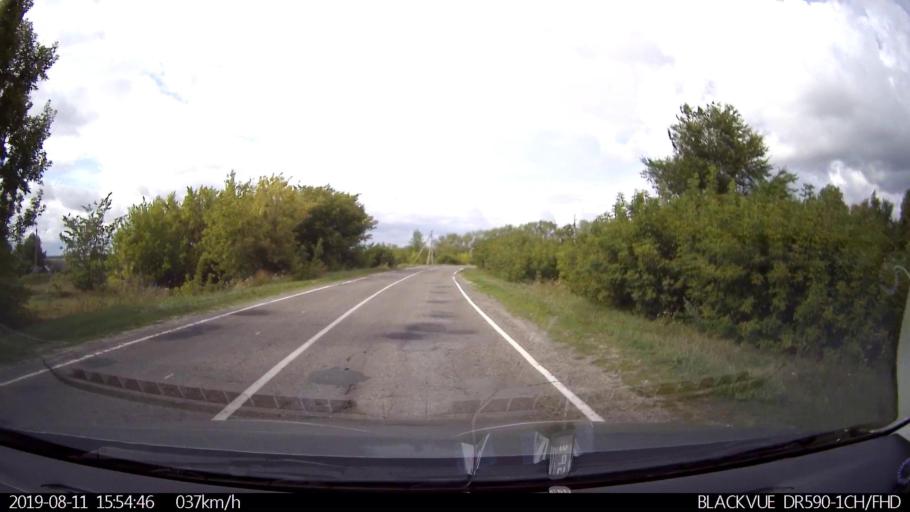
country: RU
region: Ulyanovsk
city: Ignatovka
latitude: 53.9428
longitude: 47.6560
